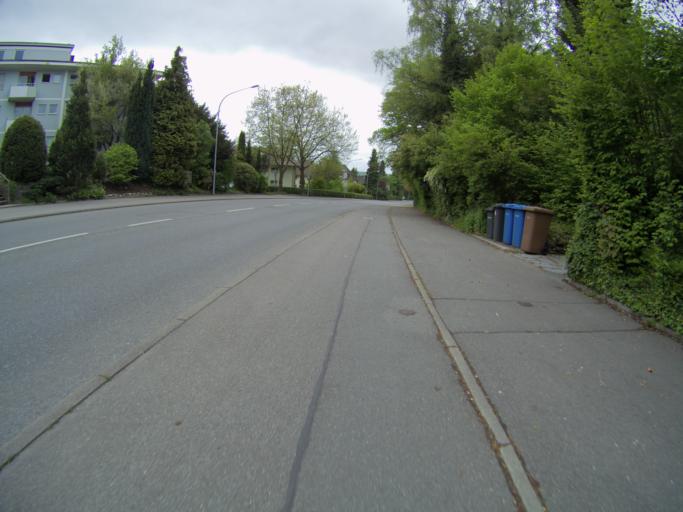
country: DE
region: Baden-Wuerttemberg
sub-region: Freiburg Region
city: Konstanz
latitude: 47.6726
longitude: 9.1923
